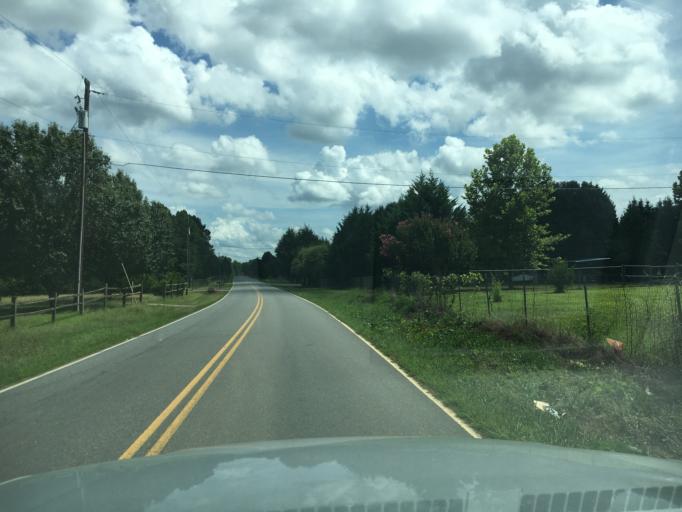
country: US
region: South Carolina
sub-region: Anderson County
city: Belton
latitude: 34.5569
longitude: -82.4685
